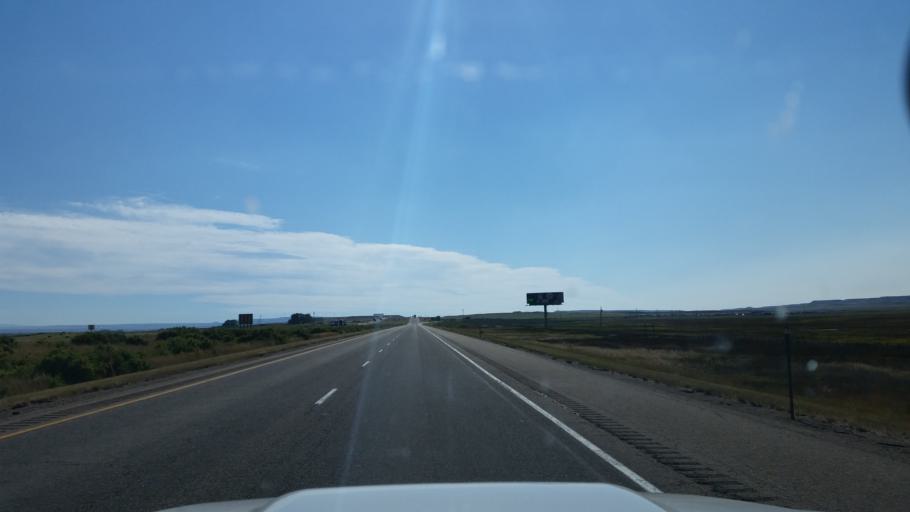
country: US
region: Wyoming
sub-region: Uinta County
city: Lyman
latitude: 41.3612
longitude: -110.3249
